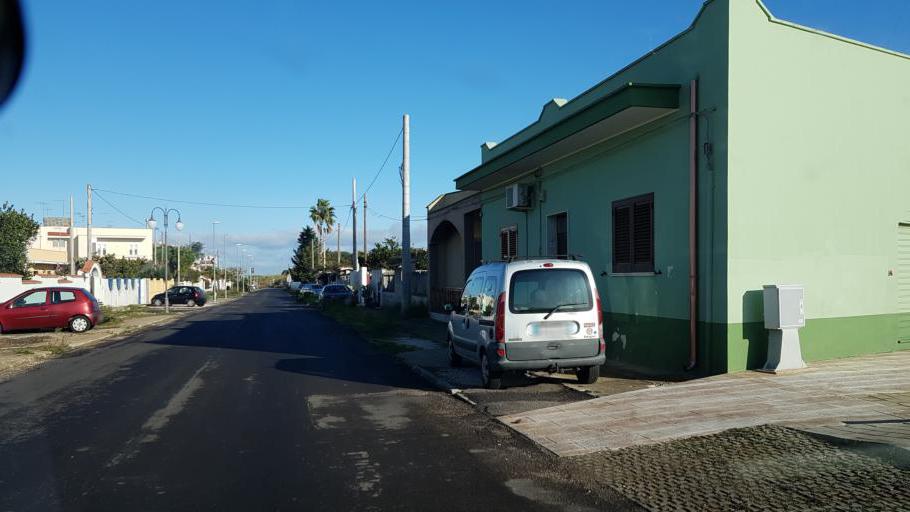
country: IT
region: Apulia
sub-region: Provincia di Brindisi
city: Tuturano
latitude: 40.5468
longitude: 17.9471
